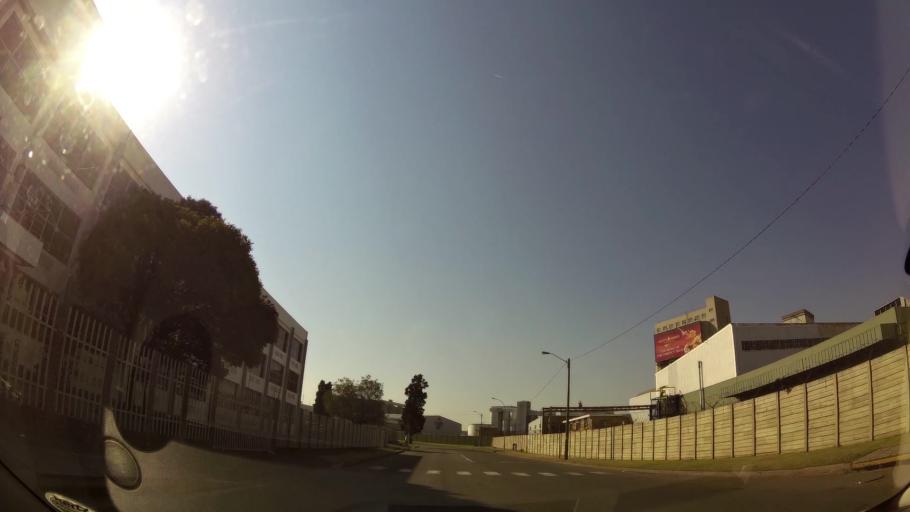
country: ZA
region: Gauteng
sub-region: City of Johannesburg Metropolitan Municipality
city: Modderfontein
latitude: -26.1484
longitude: 28.2028
